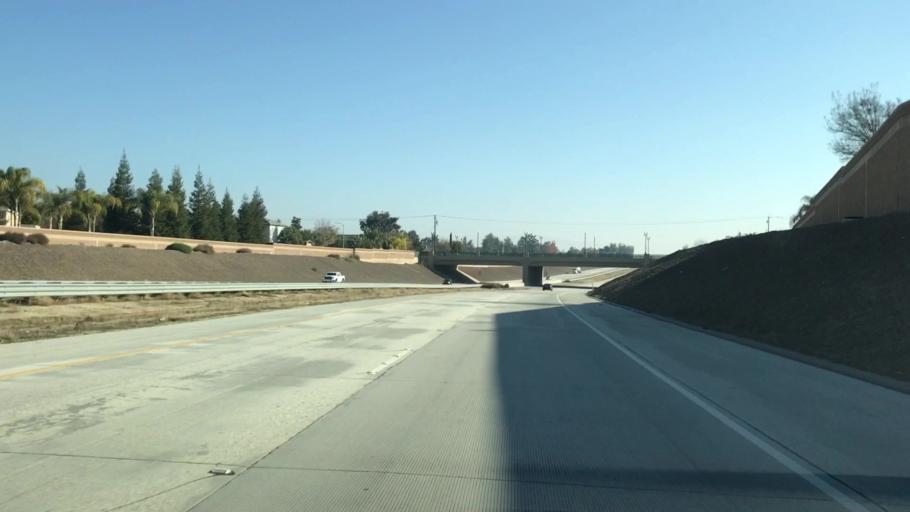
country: US
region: California
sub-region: Kern County
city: Rosedale
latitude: 35.3591
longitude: -119.1662
